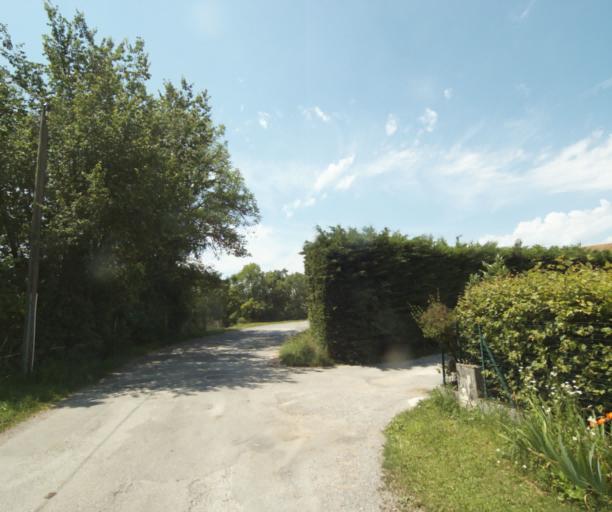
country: FR
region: Rhone-Alpes
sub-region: Departement de la Haute-Savoie
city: Messery
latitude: 46.3643
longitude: 6.3373
